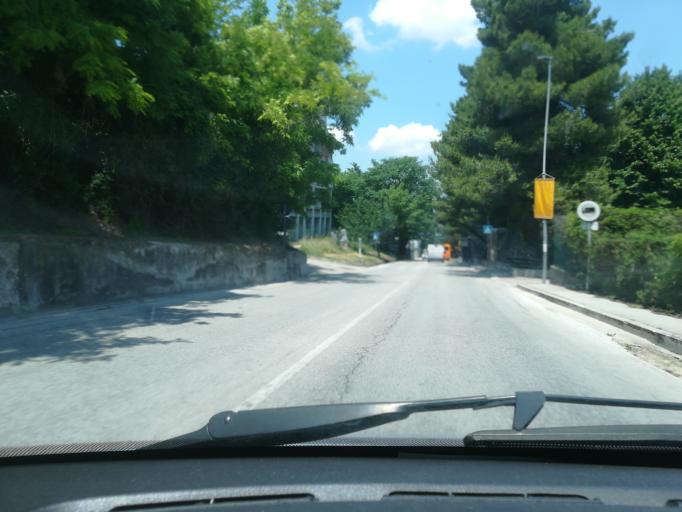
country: IT
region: The Marches
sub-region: Provincia di Macerata
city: Villa Potenza
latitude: 43.3103
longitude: 13.4359
